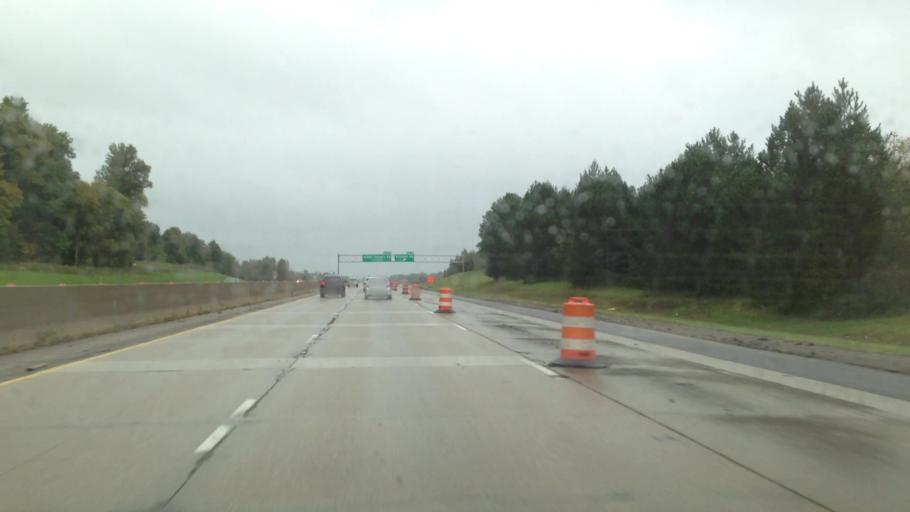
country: US
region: Ohio
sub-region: Summit County
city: Hudson
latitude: 41.2091
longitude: -81.4861
